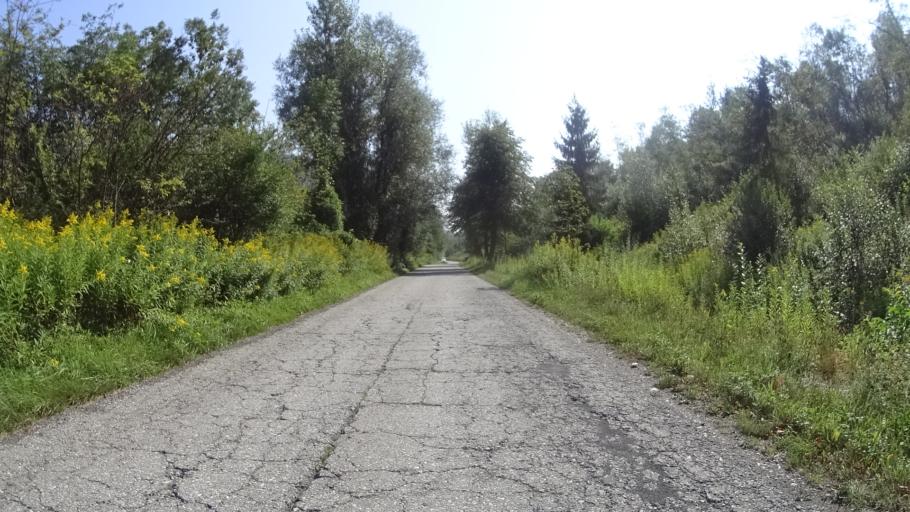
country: AT
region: Carinthia
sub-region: Politischer Bezirk Klagenfurt Land
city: Grafenstein
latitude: 46.5617
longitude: 14.4498
